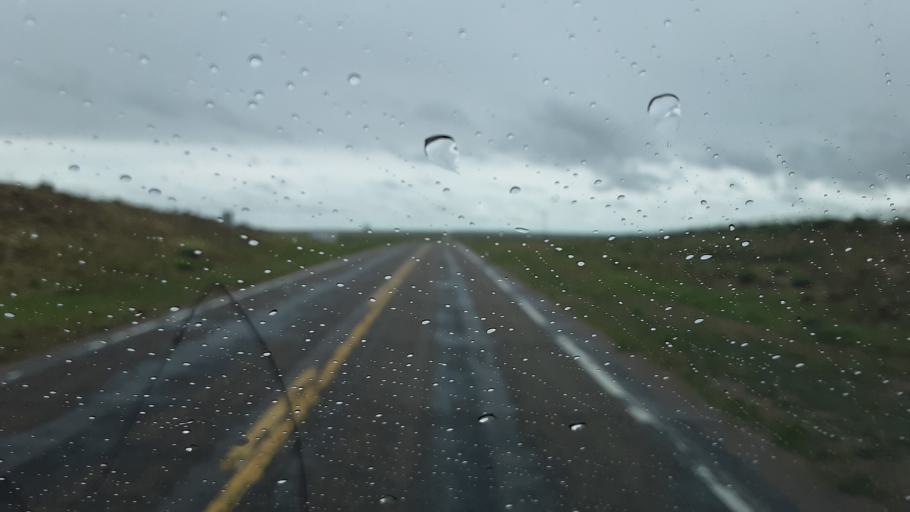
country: US
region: Colorado
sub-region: Lincoln County
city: Hugo
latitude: 38.8493
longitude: -103.2710
